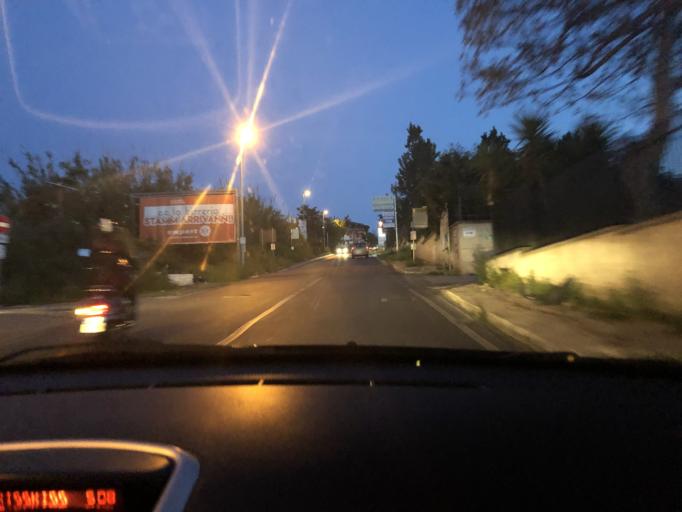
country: IT
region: Campania
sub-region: Provincia di Napoli
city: Marano di Napoli
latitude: 40.8903
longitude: 14.1790
